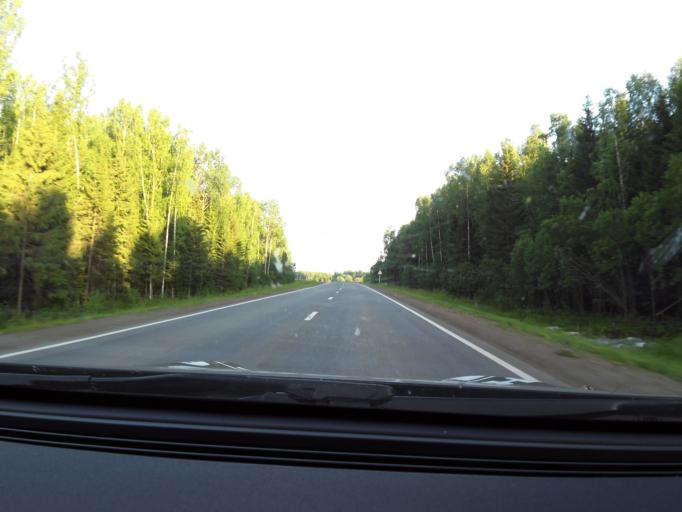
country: RU
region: Perm
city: Siva
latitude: 58.4977
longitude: 54.0469
